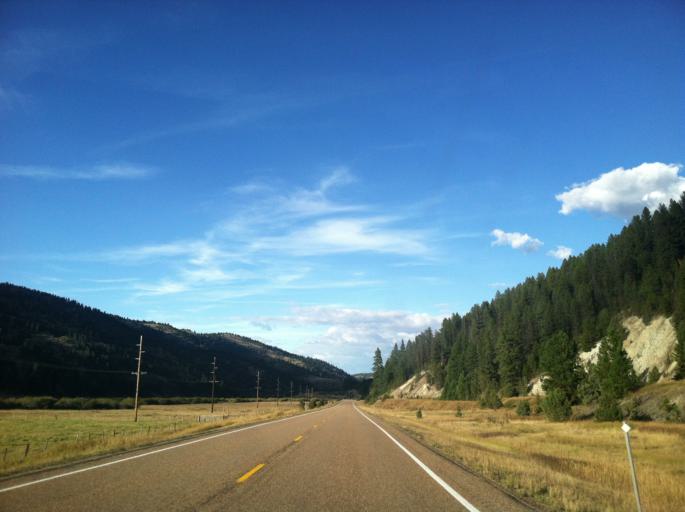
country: US
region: Montana
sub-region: Granite County
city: Philipsburg
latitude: 46.4059
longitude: -113.2938
